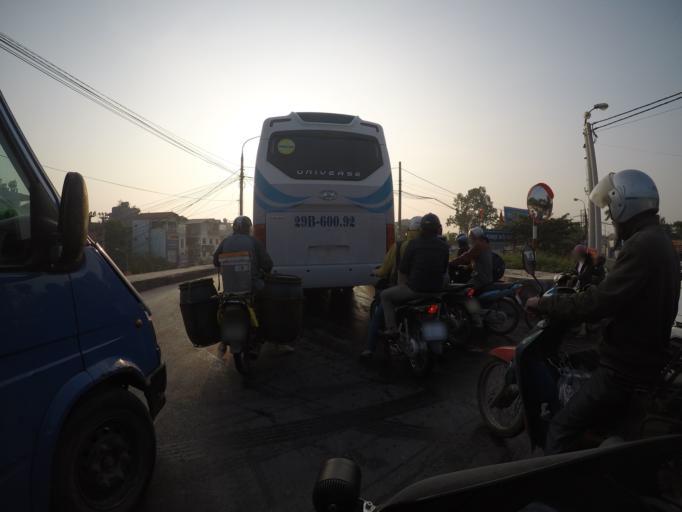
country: VN
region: Ha Noi
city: Hoan Kiem
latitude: 21.0371
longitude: 105.8699
